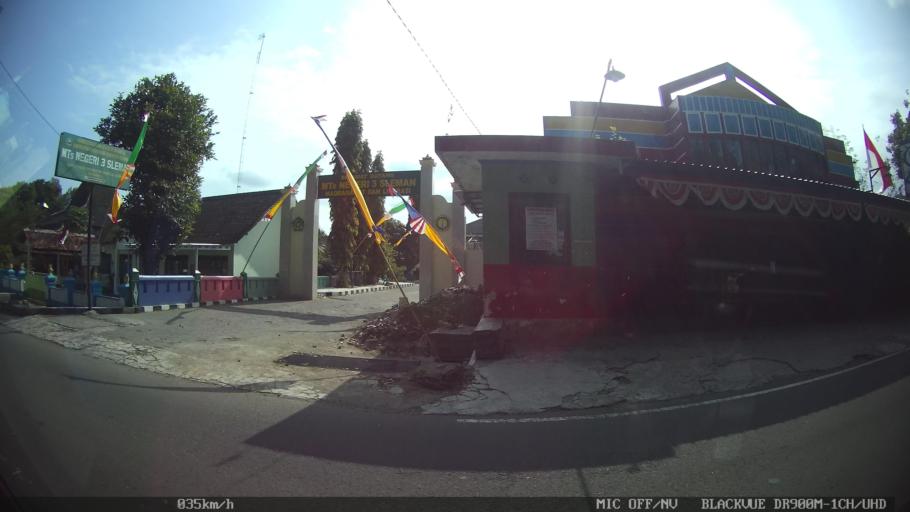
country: ID
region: Daerah Istimewa Yogyakarta
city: Depok
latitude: -7.7308
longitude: 110.4349
